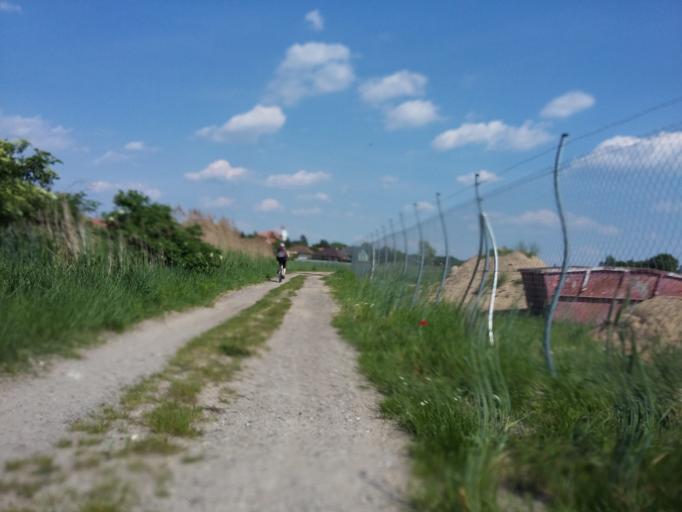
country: SK
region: Bratislavsky
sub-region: Okres Malacky
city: Malacky
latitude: 48.5007
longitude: 16.9885
